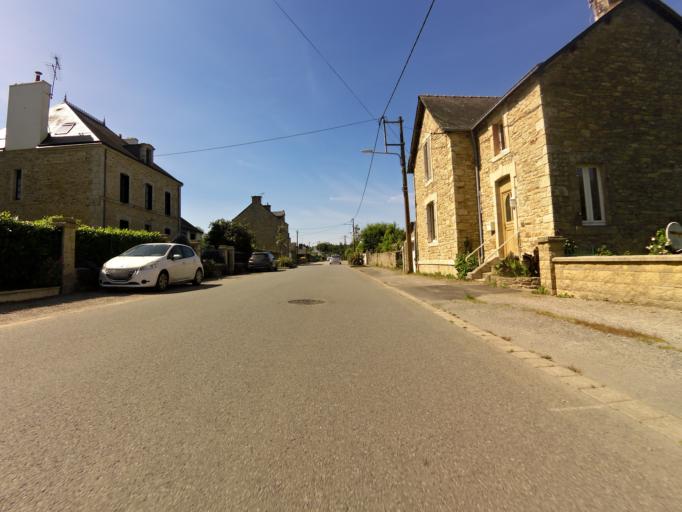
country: FR
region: Brittany
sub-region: Departement du Morbihan
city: Malansac
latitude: 47.6797
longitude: -2.2991
